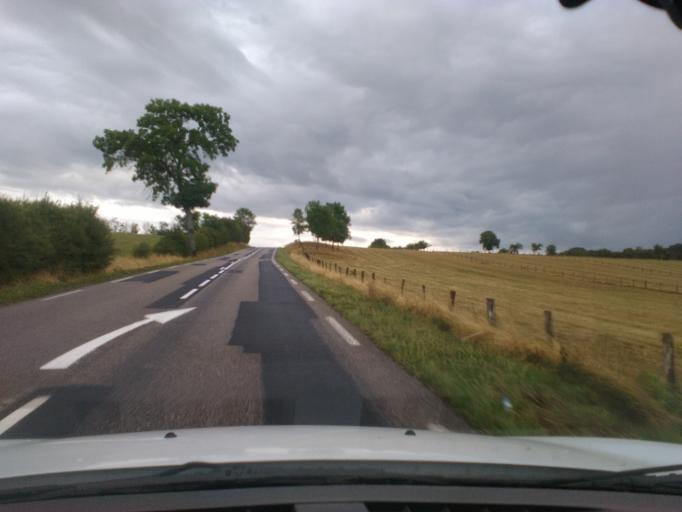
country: FR
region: Lorraine
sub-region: Departement de Meurthe-et-Moselle
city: Vezelise
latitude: 48.4278
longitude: 6.1256
